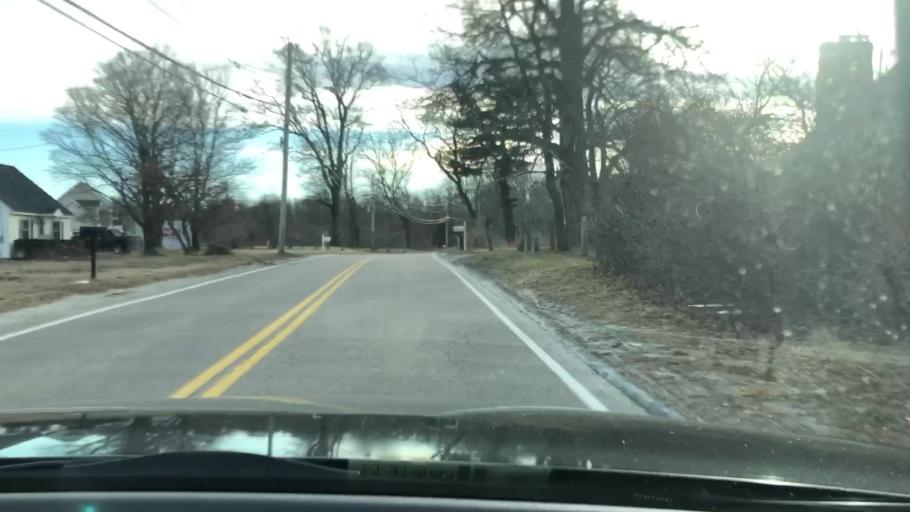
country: US
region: Massachusetts
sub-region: Worcester County
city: Blackstone
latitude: 42.0588
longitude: -71.5285
